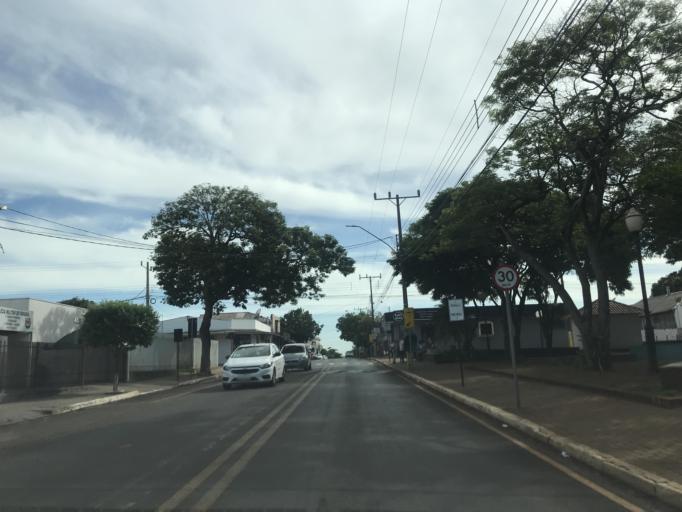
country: BR
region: Parana
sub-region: Paranavai
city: Nova Aurora
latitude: -22.9337
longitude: -52.6856
